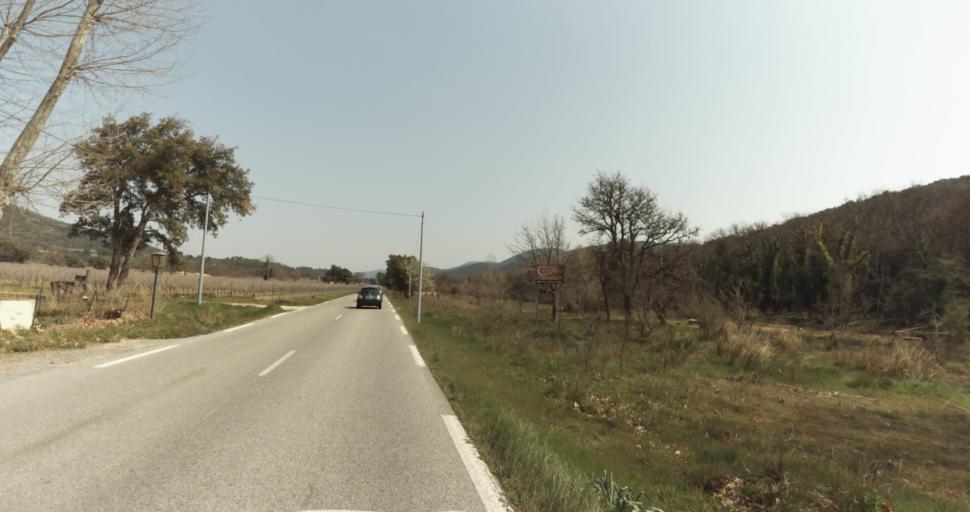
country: FR
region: Provence-Alpes-Cote d'Azur
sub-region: Departement du Var
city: Le Lavandou
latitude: 43.1996
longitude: 6.3999
